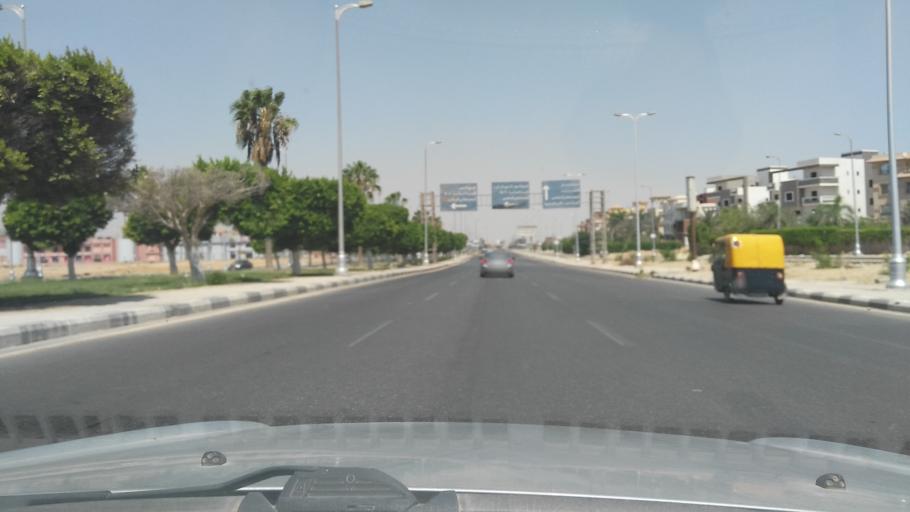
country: EG
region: Al Jizah
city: Madinat Sittah Uktubar
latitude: 29.9756
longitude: 30.9587
